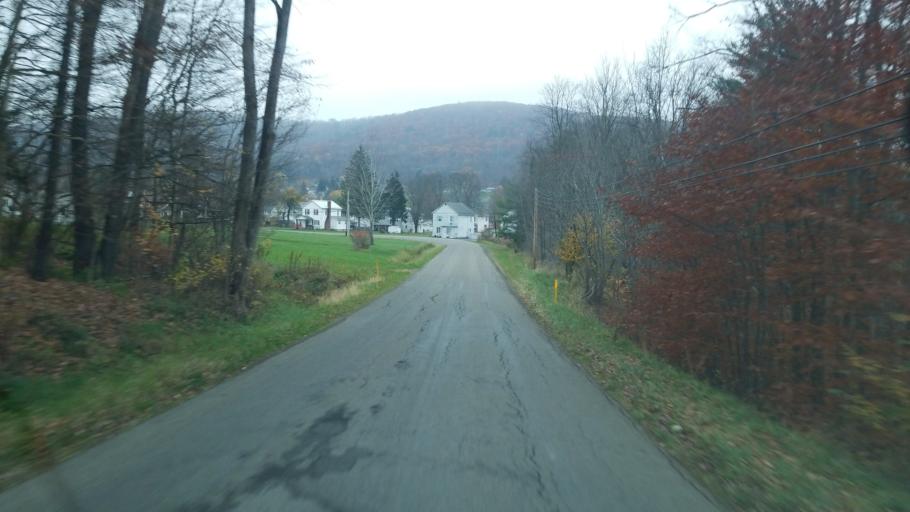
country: US
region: Pennsylvania
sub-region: McKean County
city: Smethport
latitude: 41.8050
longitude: -78.4333
